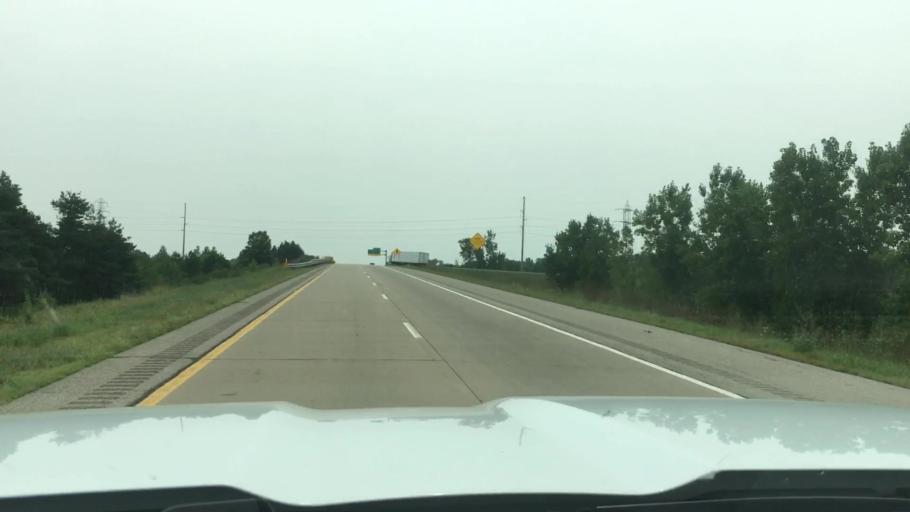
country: US
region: Michigan
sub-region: Eaton County
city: Dimondale
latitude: 42.6787
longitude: -84.6559
